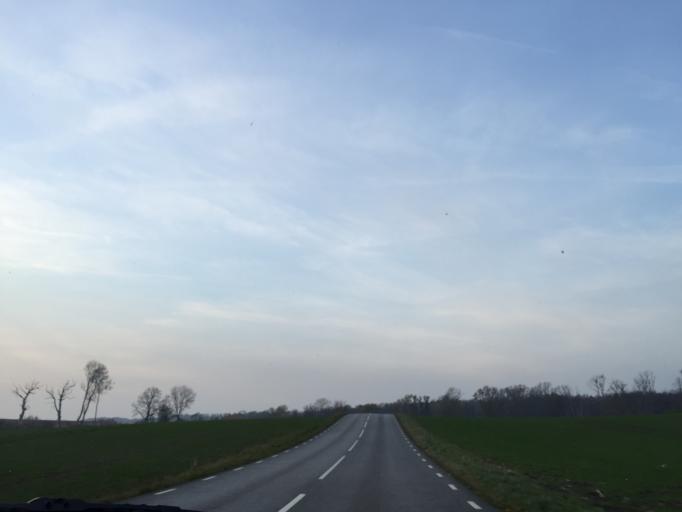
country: SE
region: Skane
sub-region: Sjobo Kommun
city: Blentarp
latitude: 55.6970
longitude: 13.6015
